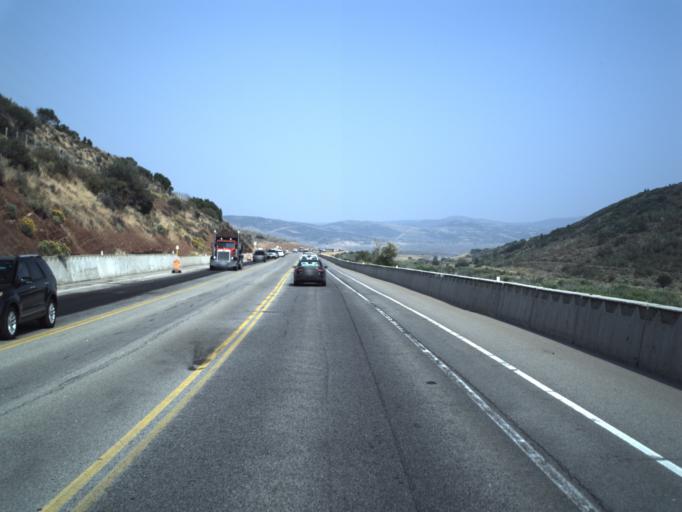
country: US
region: Utah
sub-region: Summit County
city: Park City
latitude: 40.6689
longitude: -111.4819
